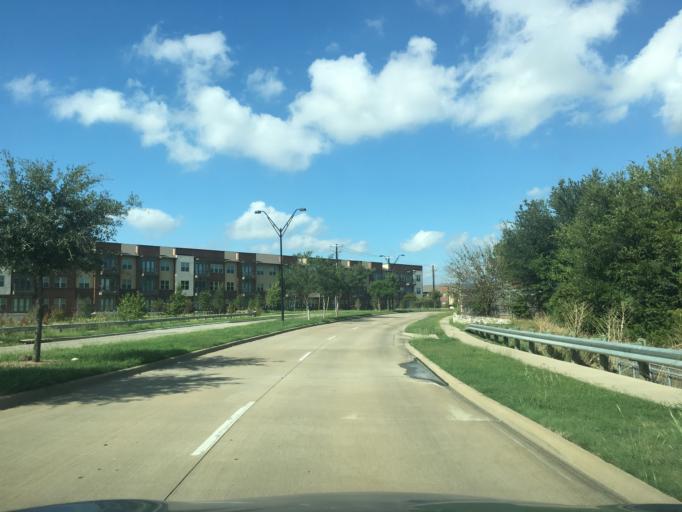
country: US
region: Texas
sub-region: Dallas County
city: Sachse
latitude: 32.9528
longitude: -96.5864
